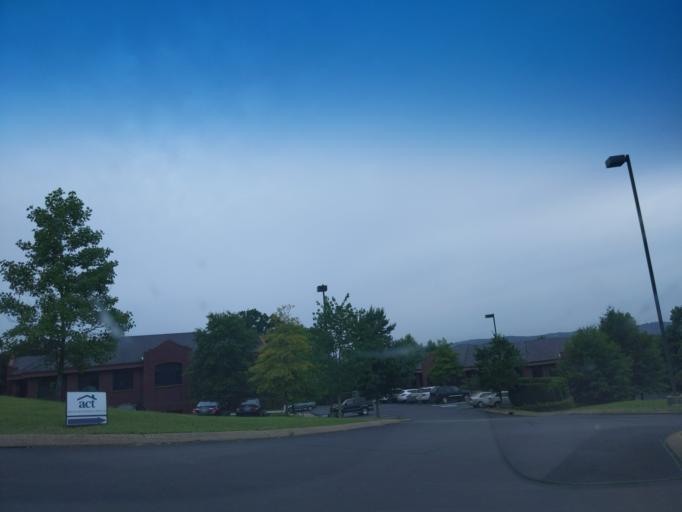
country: US
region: Tennessee
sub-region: Williamson County
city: Brentwood
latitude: 36.0313
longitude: -86.7778
